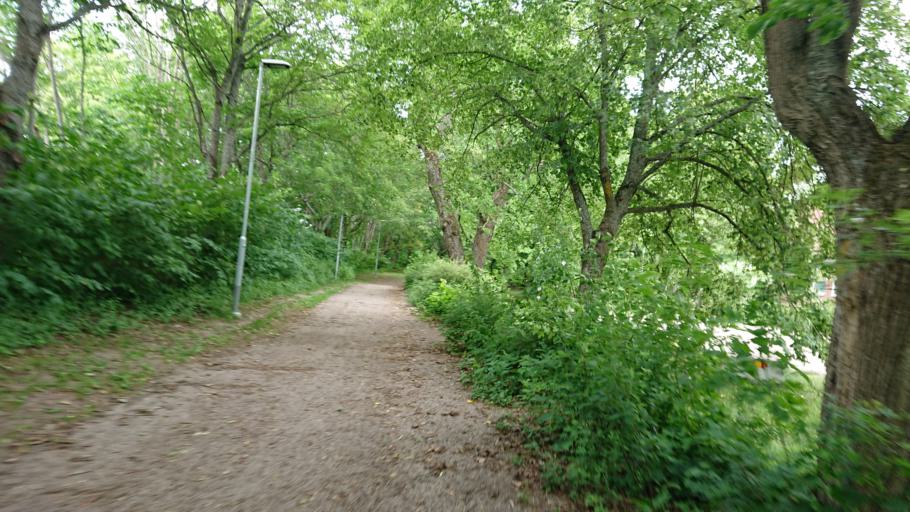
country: SE
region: Uppsala
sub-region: Uppsala Kommun
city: Gamla Uppsala
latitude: 59.8770
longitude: 17.6146
